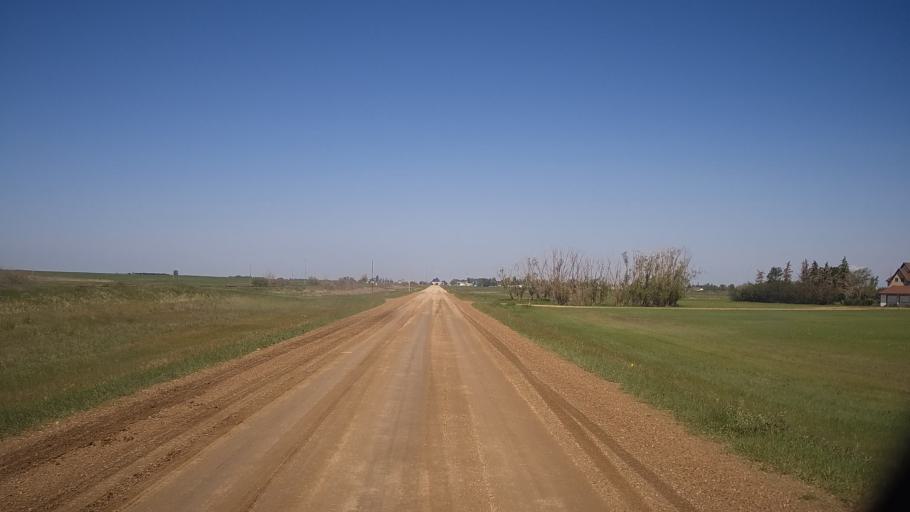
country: CA
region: Saskatchewan
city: Watrous
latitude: 51.8851
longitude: -106.0344
